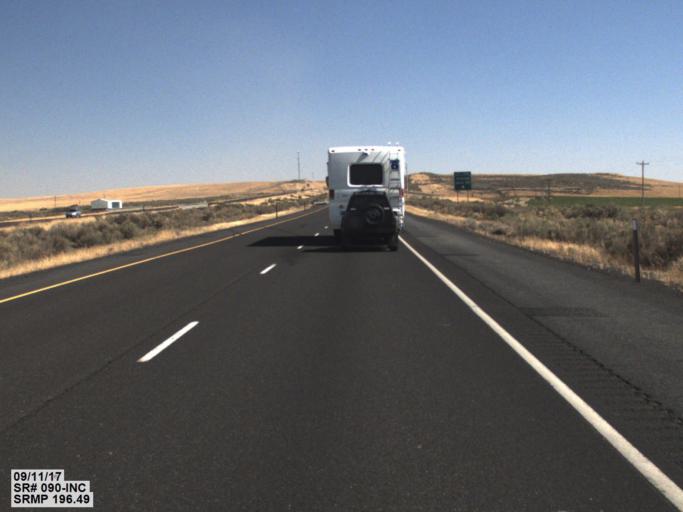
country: US
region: Washington
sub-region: Grant County
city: Warden
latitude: 47.0869
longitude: -118.8840
